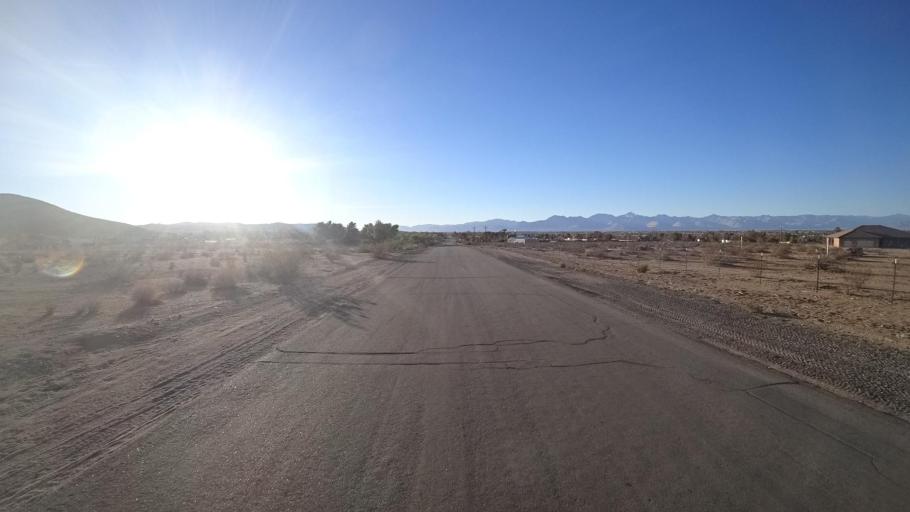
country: US
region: California
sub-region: Kern County
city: Ridgecrest
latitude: 35.5861
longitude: -117.6509
